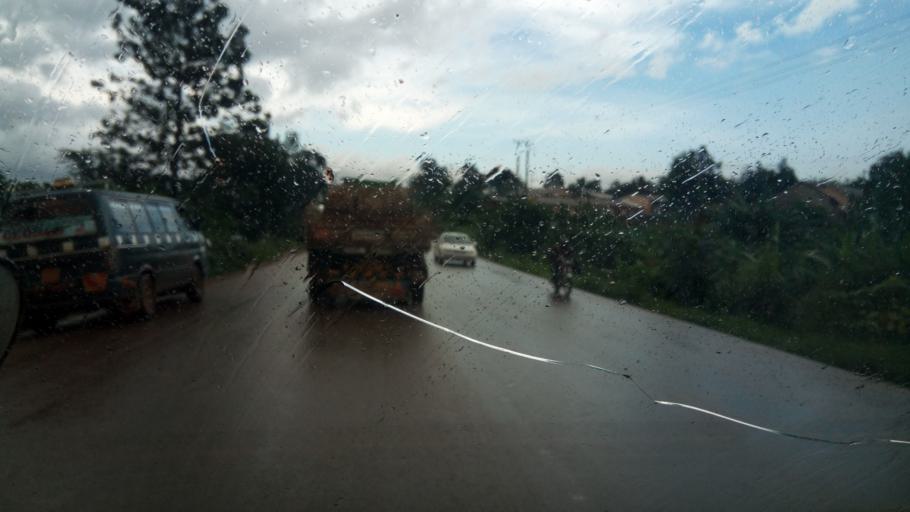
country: UG
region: Central Region
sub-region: Wakiso District
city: Wakiso
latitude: 0.3968
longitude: 32.4891
